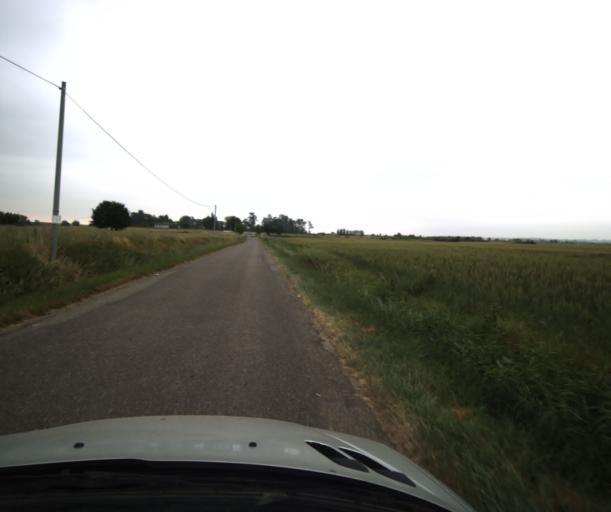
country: FR
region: Midi-Pyrenees
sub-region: Departement du Tarn-et-Garonne
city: Saint-Nicolas-de-la-Grave
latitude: 44.0473
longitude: 1.0267
